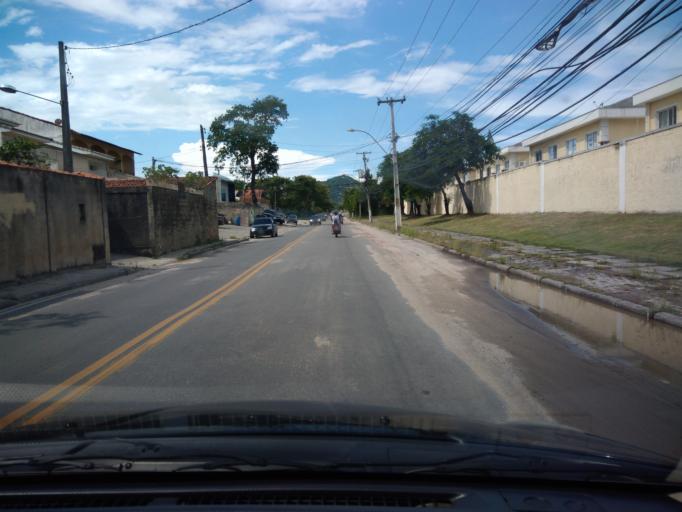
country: BR
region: Rio de Janeiro
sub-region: Niteroi
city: Niteroi
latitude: -22.9439
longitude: -43.0198
